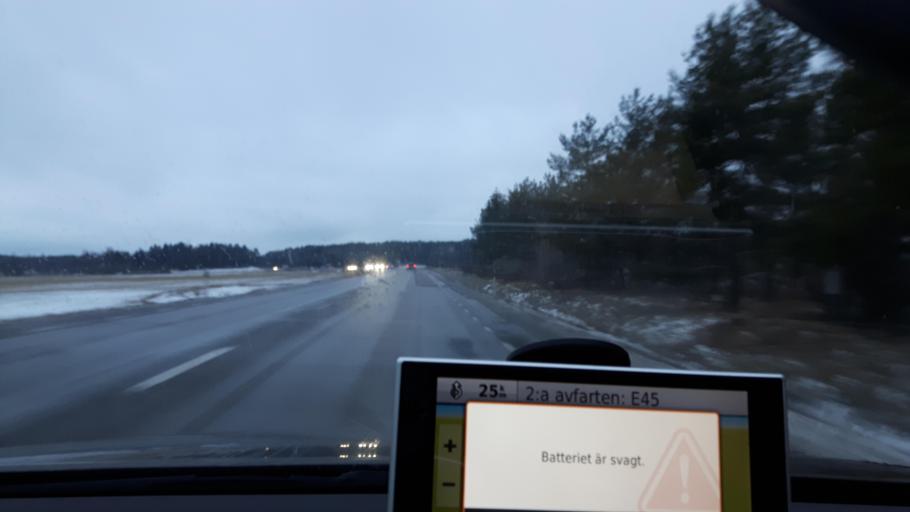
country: SE
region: Vaermland
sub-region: Saffle Kommun
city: Saeffle
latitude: 59.1788
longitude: 13.0092
